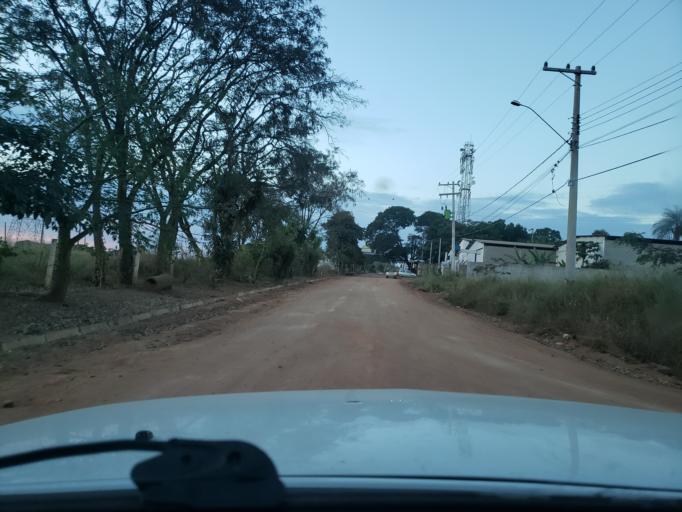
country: BR
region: Sao Paulo
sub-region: Mogi-Mirim
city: Mogi Mirim
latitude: -22.4931
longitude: -46.9818
